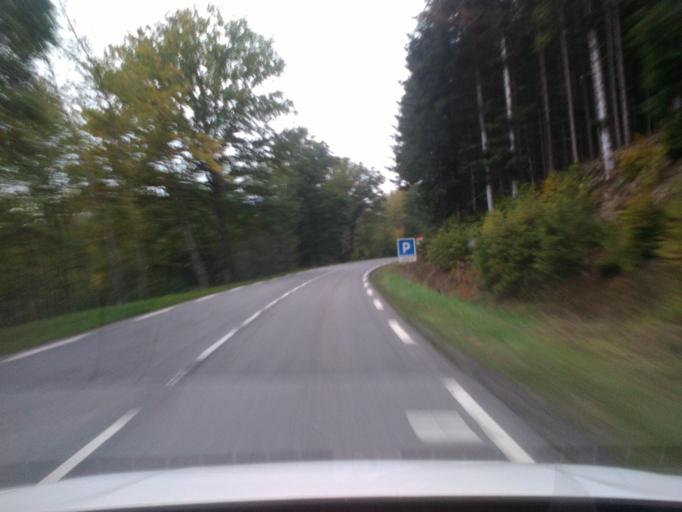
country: FR
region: Lorraine
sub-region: Departement des Vosges
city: Ban-de-Laveline
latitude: 48.3218
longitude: 7.0936
